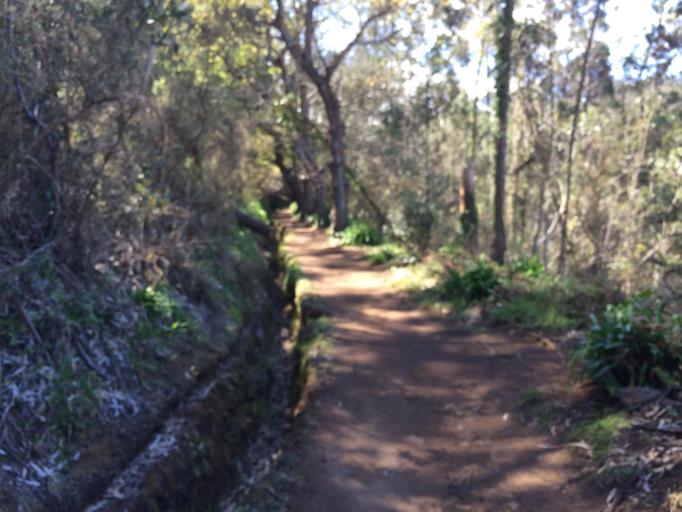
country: PT
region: Madeira
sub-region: Santa Cruz
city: Camacha
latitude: 32.6789
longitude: -16.8542
